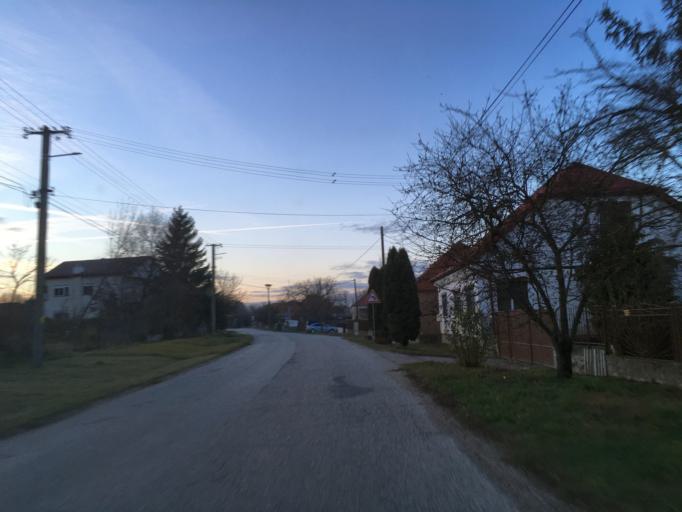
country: SK
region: Nitriansky
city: Svodin
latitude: 47.8741
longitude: 18.4549
